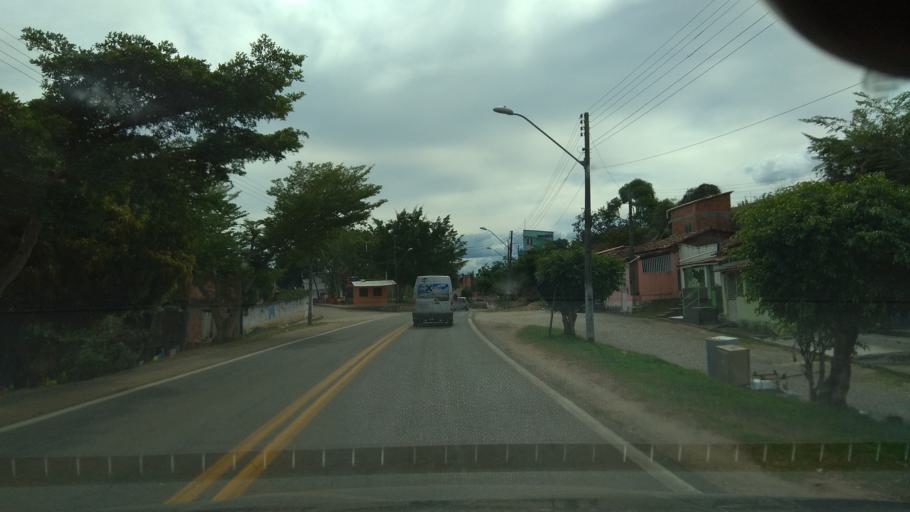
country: BR
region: Bahia
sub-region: Ubata
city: Ubata
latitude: -14.2071
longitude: -39.6025
